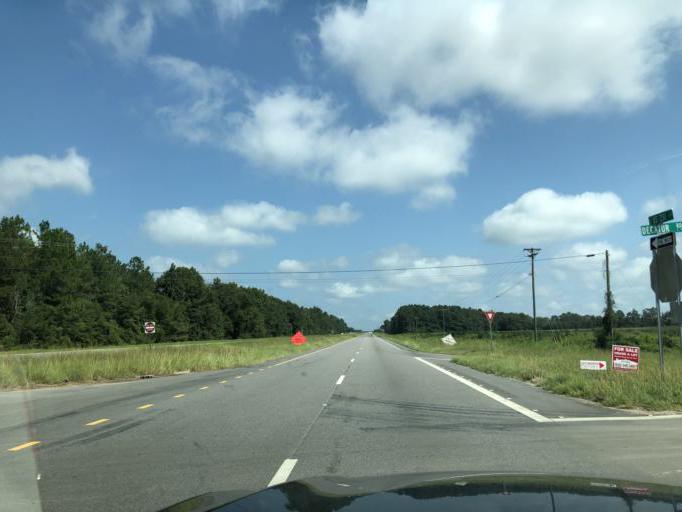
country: US
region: Alabama
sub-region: Houston County
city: Rehobeth
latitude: 31.0342
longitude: -85.4065
